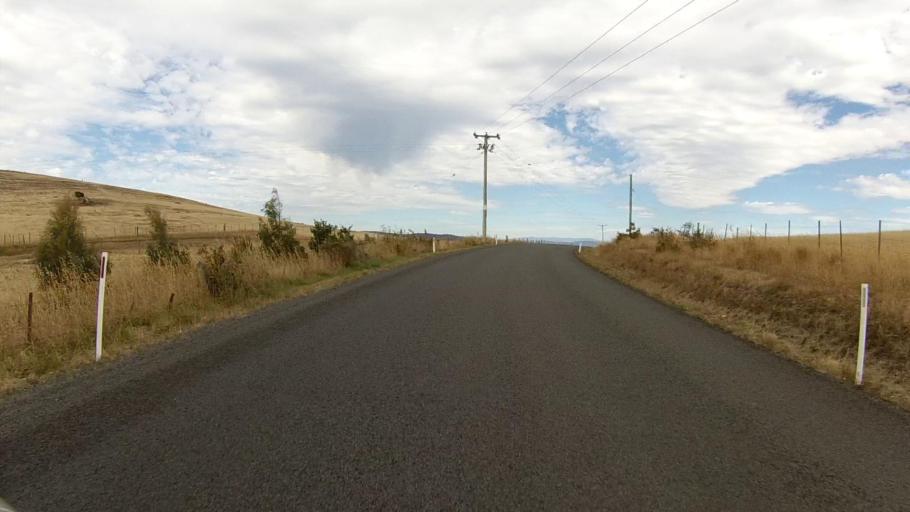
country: AU
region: Tasmania
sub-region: Sorell
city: Sorell
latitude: -42.8990
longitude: 147.7673
